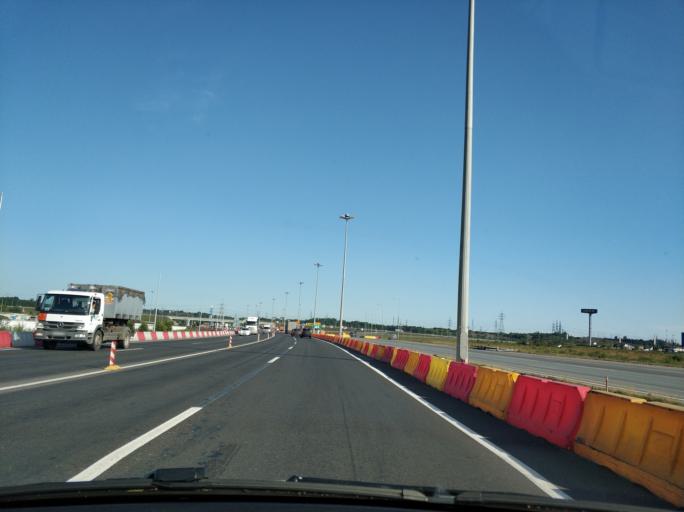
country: RU
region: Leningrad
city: Bugry
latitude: 60.0876
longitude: 30.3753
